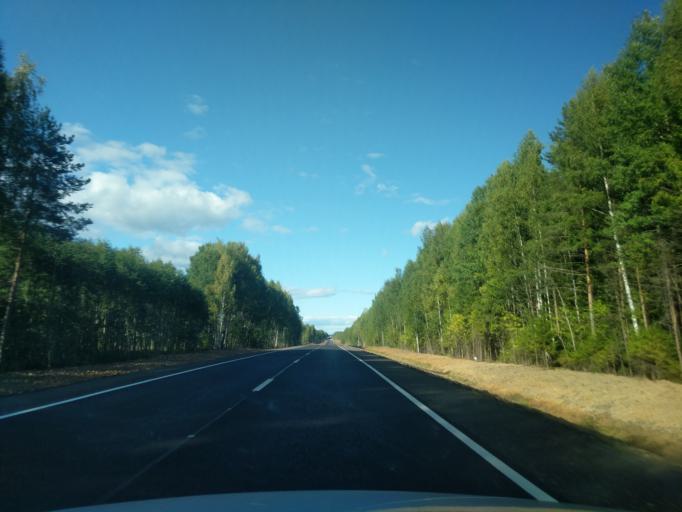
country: RU
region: Kostroma
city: Makar'yev
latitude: 57.9804
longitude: 43.9571
